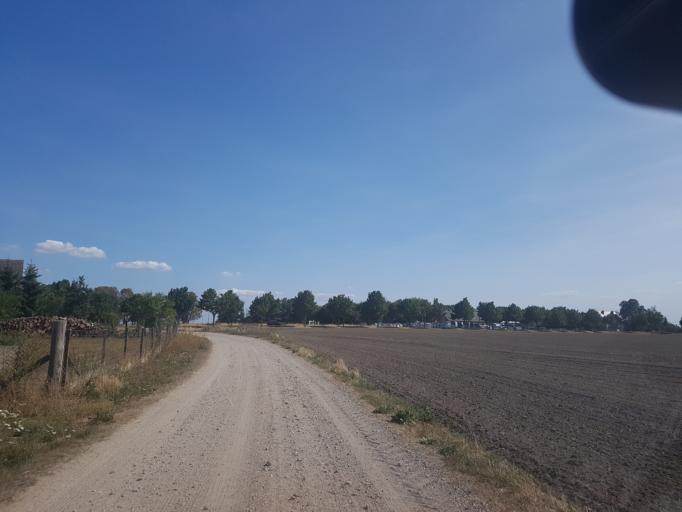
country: DE
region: Saxony-Anhalt
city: Kropstadt
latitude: 52.0163
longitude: 12.7888
